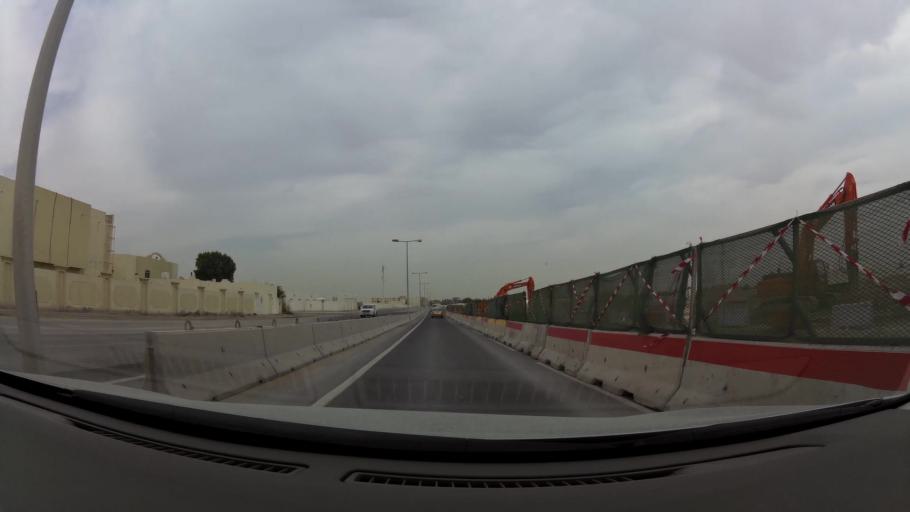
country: QA
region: Baladiyat ar Rayyan
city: Ar Rayyan
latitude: 25.2218
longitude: 51.4463
